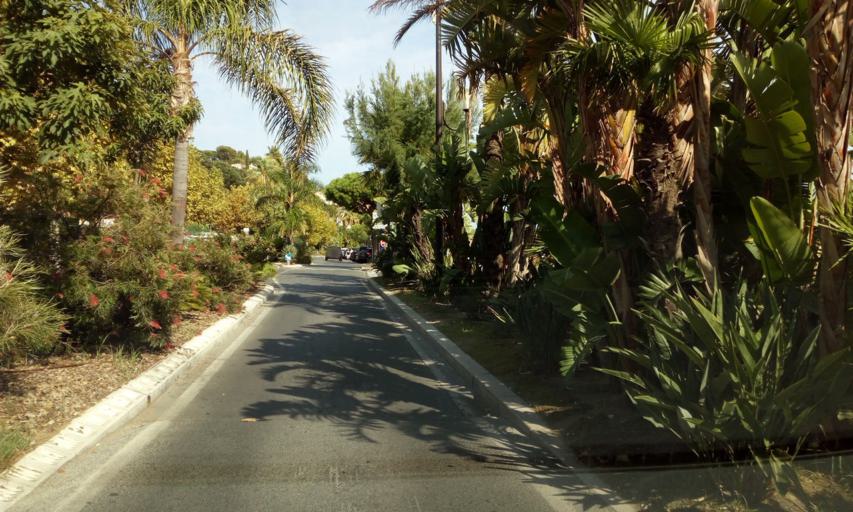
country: FR
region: Provence-Alpes-Cote d'Azur
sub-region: Departement du Var
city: Le Lavandou
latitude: 43.1379
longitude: 6.3709
